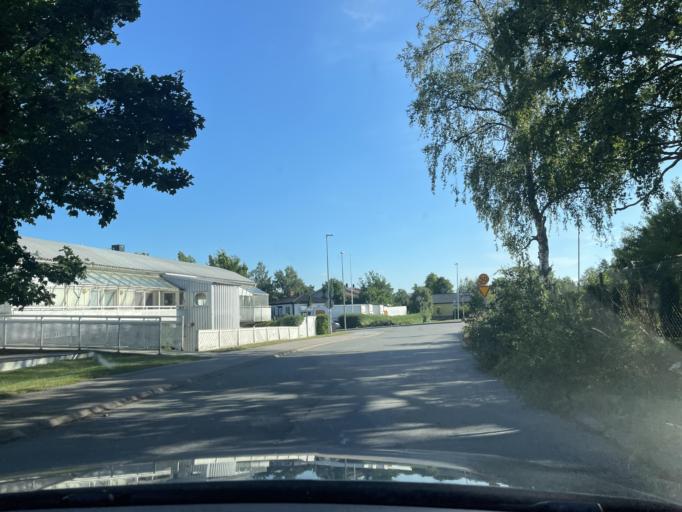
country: SE
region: Stockholm
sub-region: Sigtuna Kommun
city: Marsta
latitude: 59.6246
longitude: 17.8495
